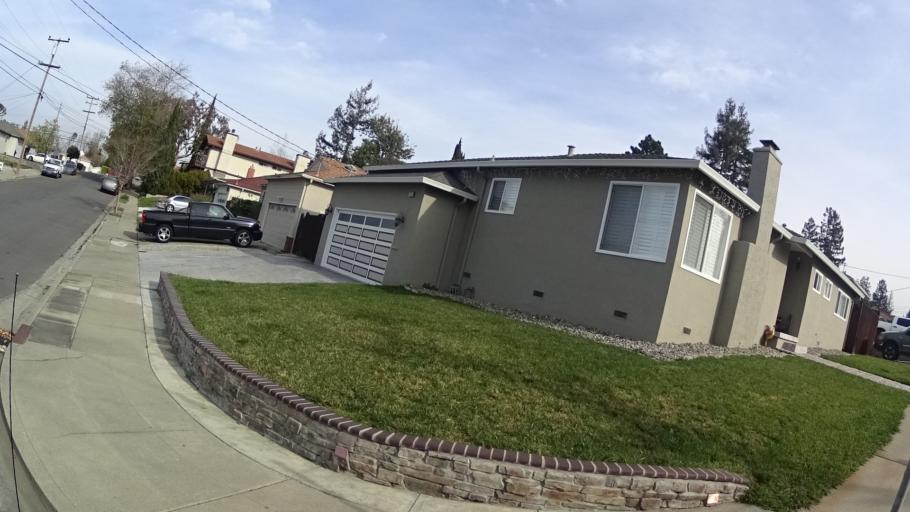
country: US
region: California
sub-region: Alameda County
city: Fairview
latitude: 37.6782
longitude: -122.0540
